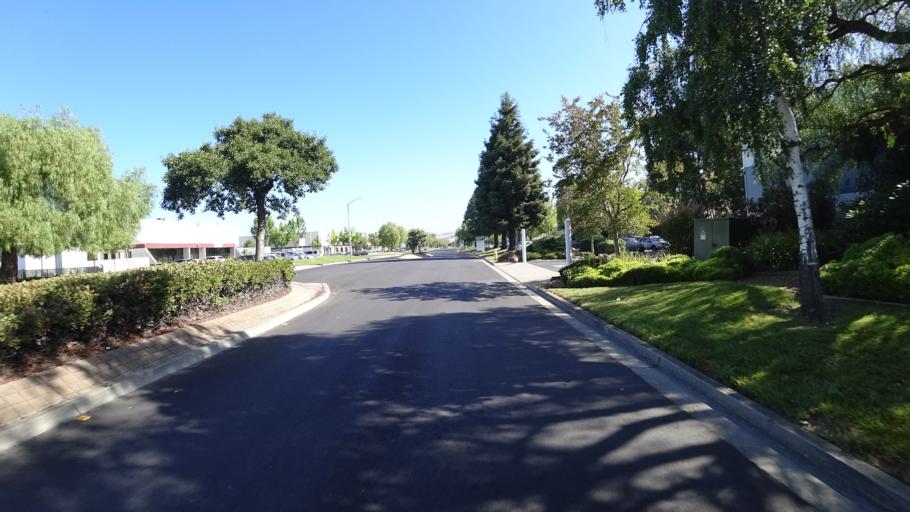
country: US
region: California
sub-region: Alameda County
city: Union City
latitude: 37.6120
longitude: -122.0525
